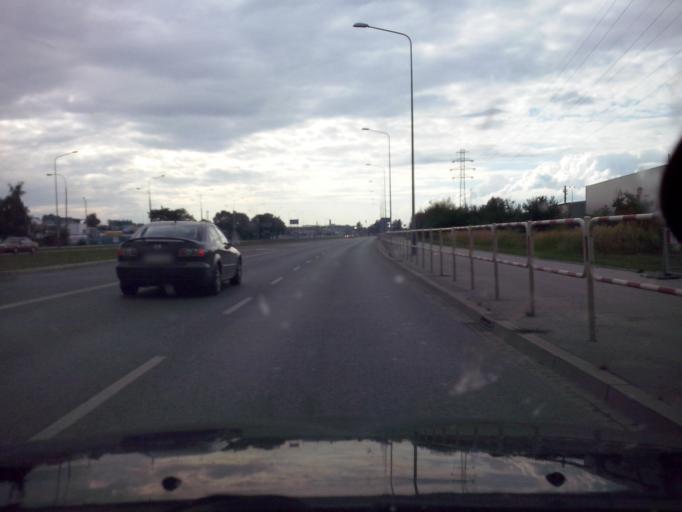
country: PL
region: Lesser Poland Voivodeship
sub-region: Powiat wielicki
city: Czarnochowice
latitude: 50.0379
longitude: 20.0241
